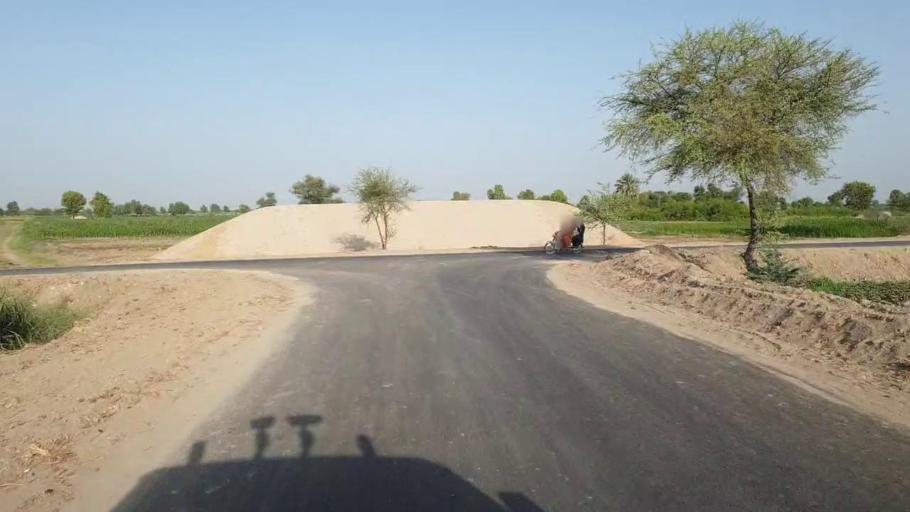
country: PK
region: Sindh
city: Jam Sahib
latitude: 26.3474
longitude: 68.5687
